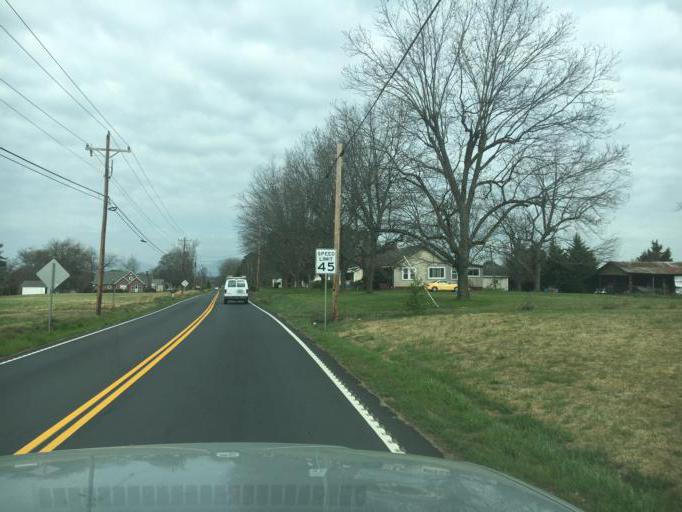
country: US
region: South Carolina
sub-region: Spartanburg County
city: Inman Mills
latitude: 35.0510
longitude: -82.1397
